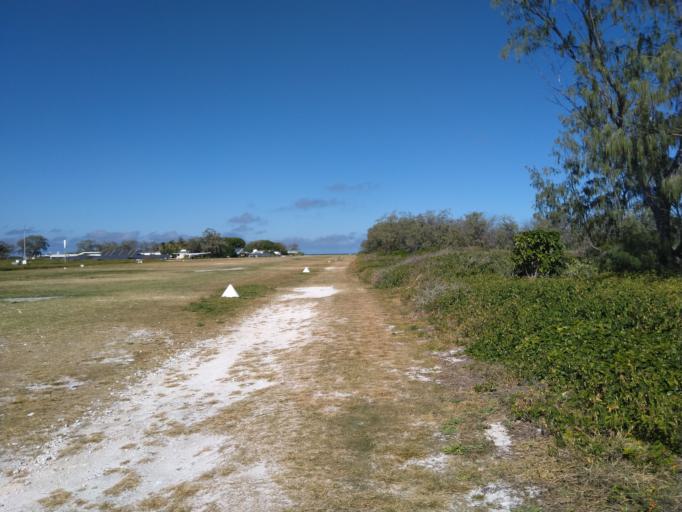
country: AU
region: Queensland
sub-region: Bundaberg
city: Bundaberg
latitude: -24.1103
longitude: 152.7154
